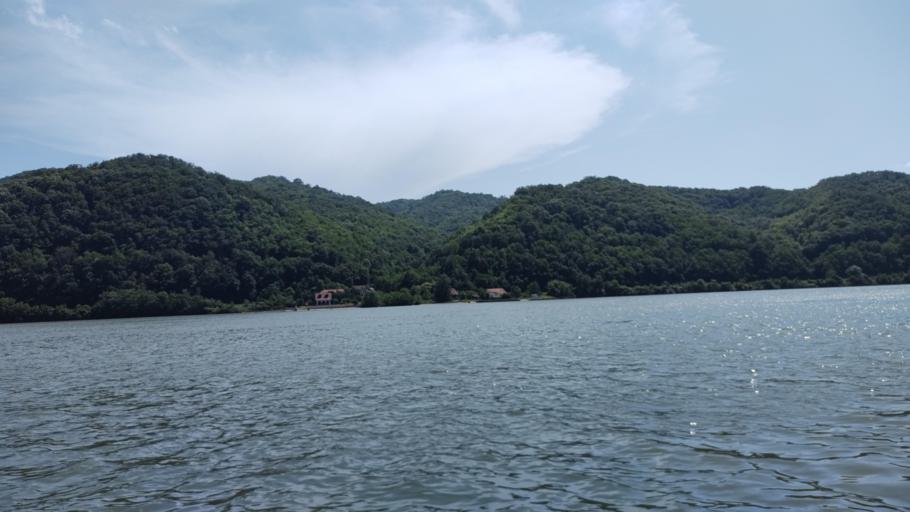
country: RS
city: Radenka
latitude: 44.6594
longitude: 21.7897
